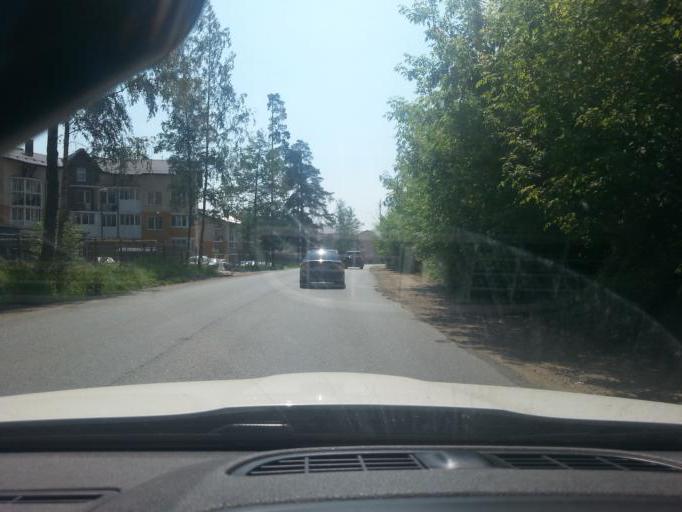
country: RU
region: Moskovskaya
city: Zheleznodorozhnyy
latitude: 55.7162
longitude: 37.9732
